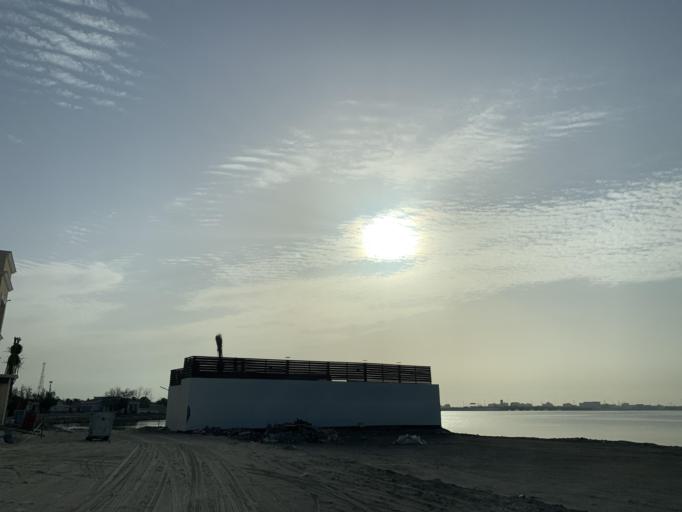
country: BH
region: Northern
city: Madinat `Isa
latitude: 26.1767
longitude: 50.5820
